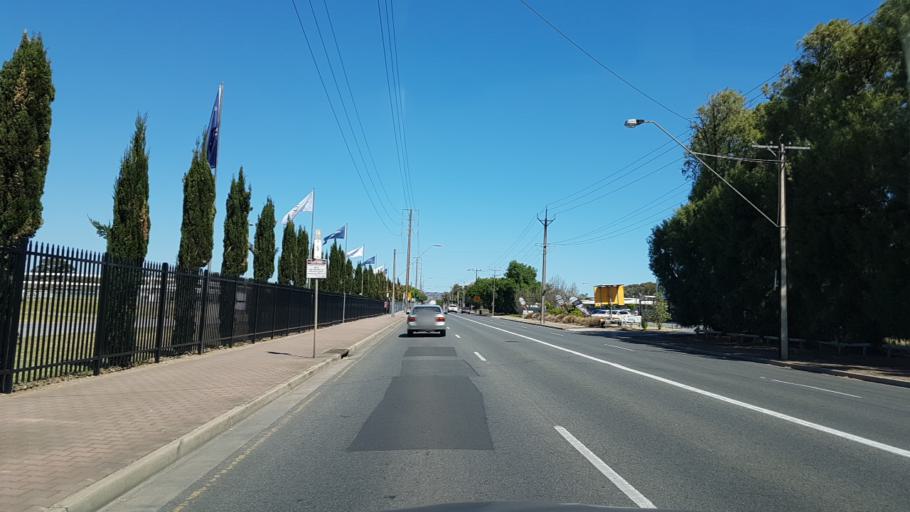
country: AU
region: South Australia
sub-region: Holdfast Bay
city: Glenelg East
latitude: -34.9784
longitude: 138.5380
